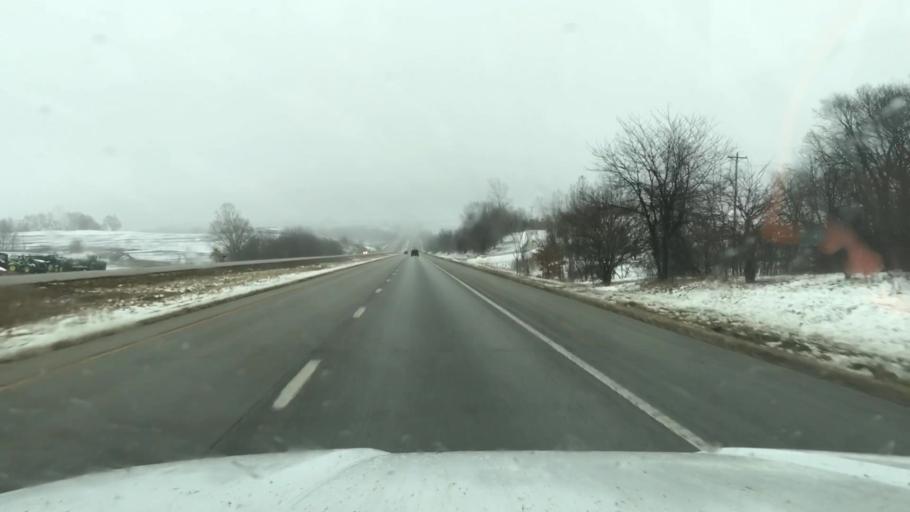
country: US
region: Missouri
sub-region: Clinton County
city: Gower
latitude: 39.7475
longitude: -94.6821
